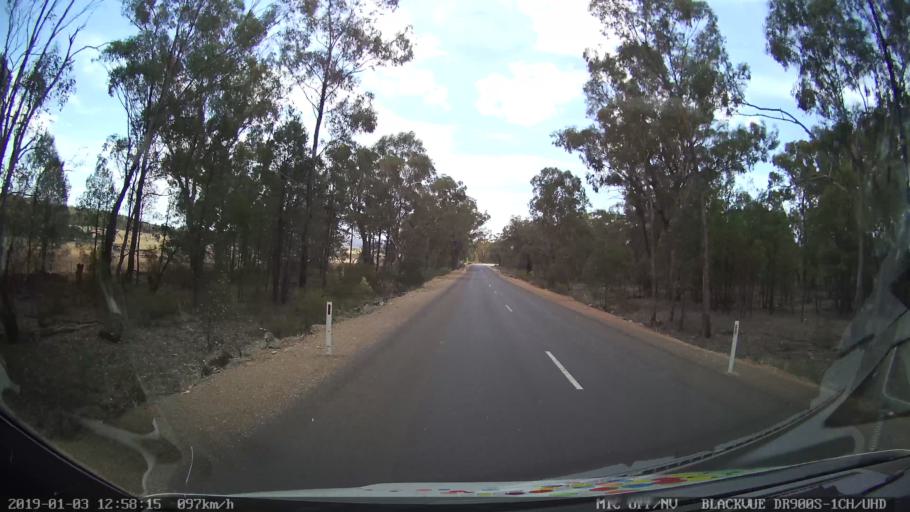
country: AU
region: New South Wales
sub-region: Cabonne
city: Canowindra
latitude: -33.6437
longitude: 148.3726
